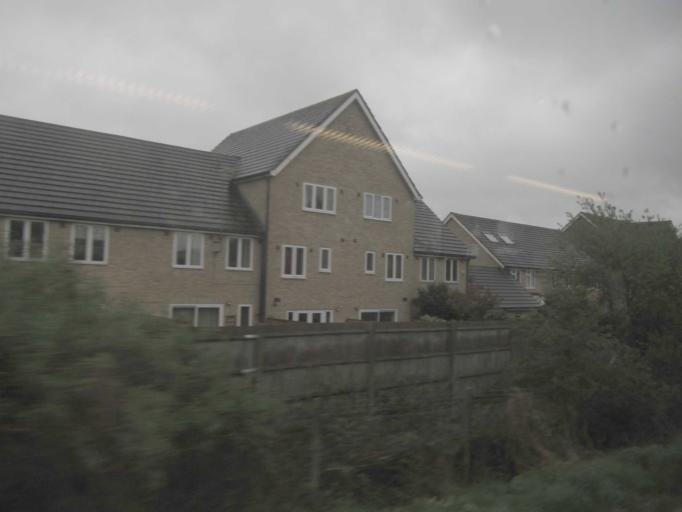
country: GB
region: England
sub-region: Wokingham
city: Wokingham
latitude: 51.4057
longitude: -0.8400
